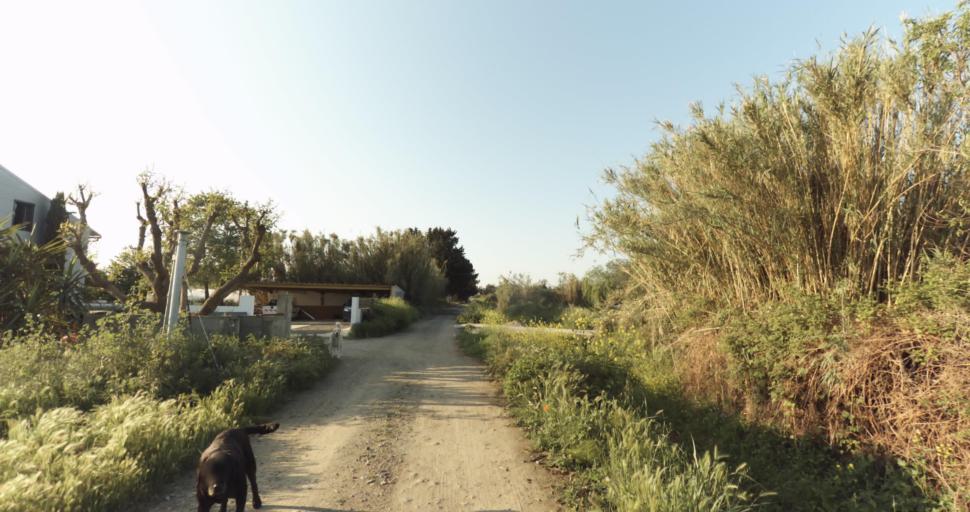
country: FR
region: Corsica
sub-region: Departement de la Haute-Corse
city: Biguglia
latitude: 42.6131
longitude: 9.4464
